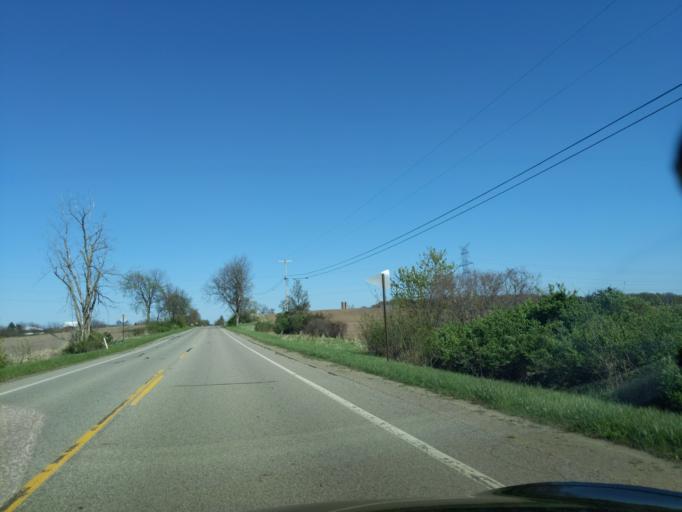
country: US
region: Michigan
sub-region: Kent County
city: Forest Hills
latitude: 42.8853
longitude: -85.4280
